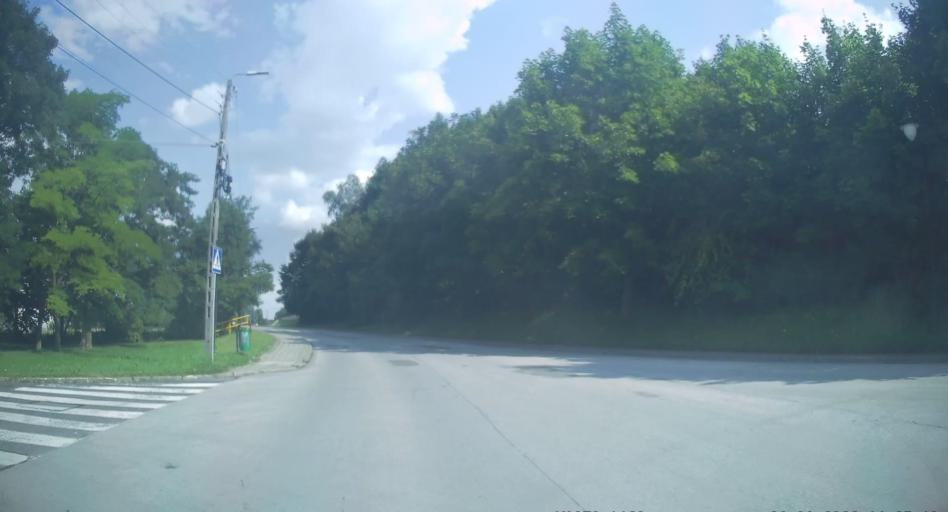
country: PL
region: Swietokrzyskie
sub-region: Powiat kielecki
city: Checiny
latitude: 50.8032
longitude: 20.4504
